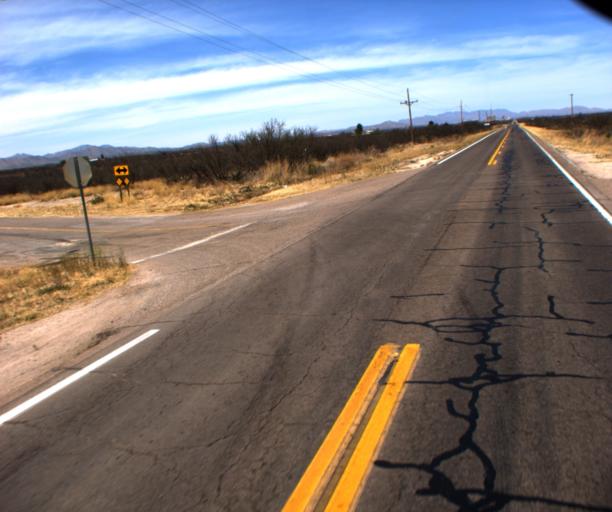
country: US
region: Arizona
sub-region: Cochise County
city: Willcox
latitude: 32.0068
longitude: -109.8643
